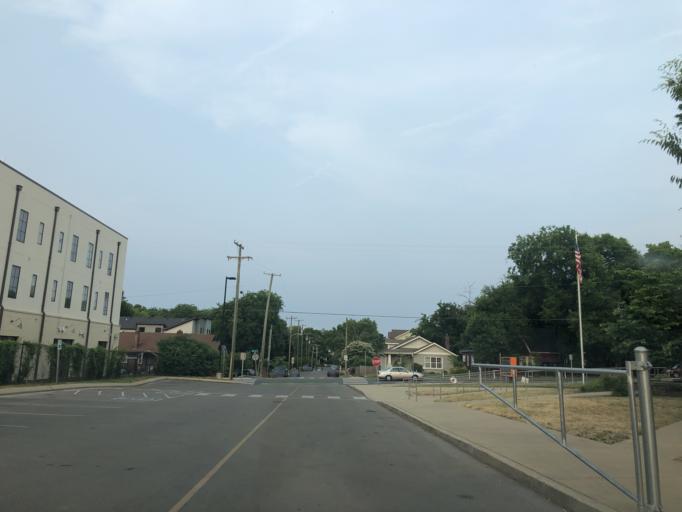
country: US
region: Tennessee
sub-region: Davidson County
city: Nashville
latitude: 36.1268
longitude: -86.7869
